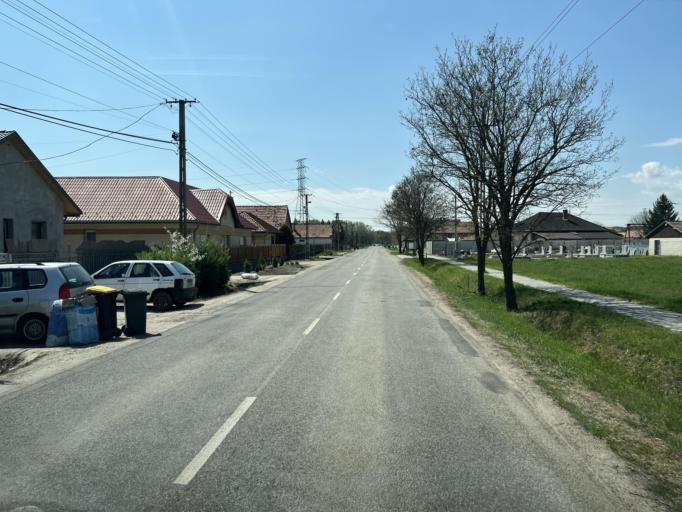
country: HU
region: Pest
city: Dabas
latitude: 47.2245
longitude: 19.2905
